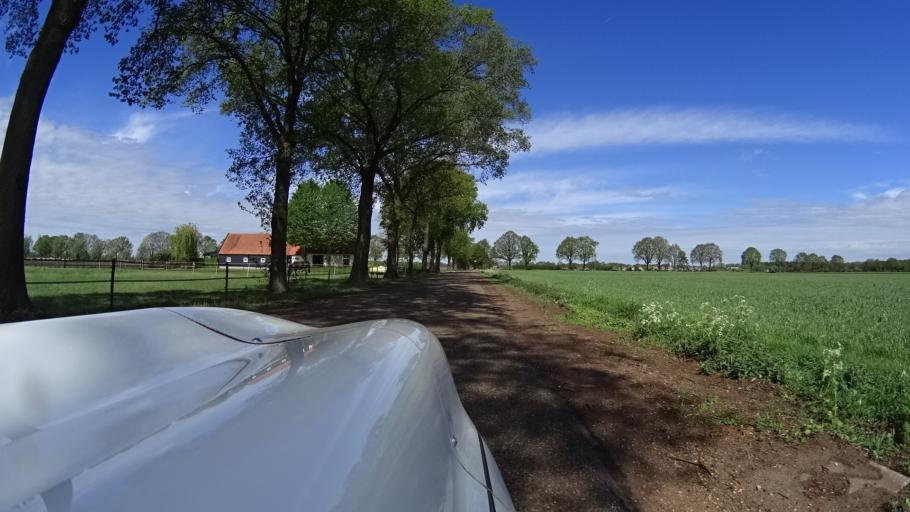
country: NL
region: North Brabant
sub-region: Gemeente Mill en Sint Hubert
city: Wilbertoord
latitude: 51.6080
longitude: 5.7955
